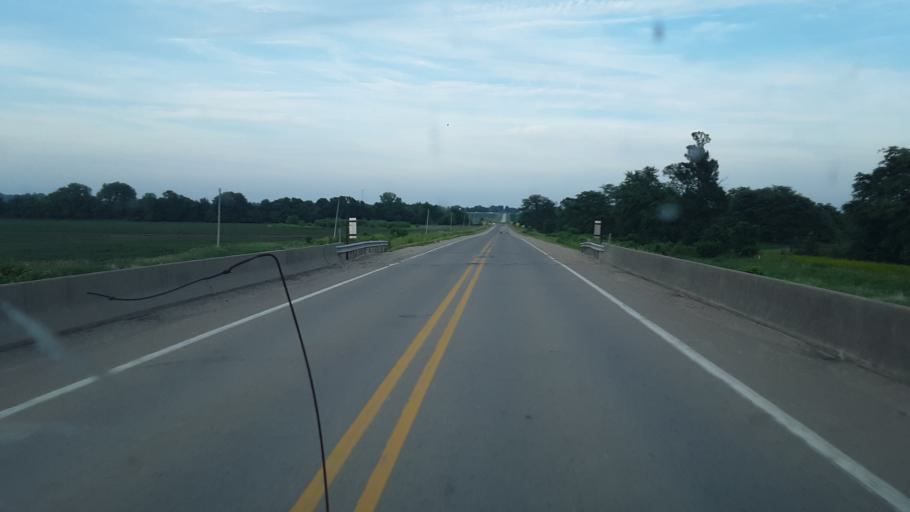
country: US
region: Iowa
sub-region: Benton County
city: Belle Plaine
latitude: 41.9063
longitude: -92.3057
